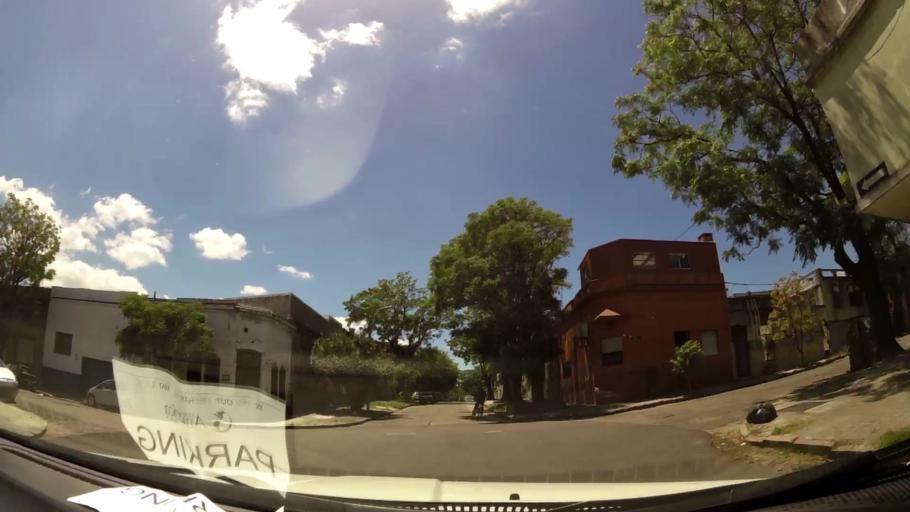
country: UY
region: Montevideo
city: Montevideo
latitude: -34.8811
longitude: -56.1746
